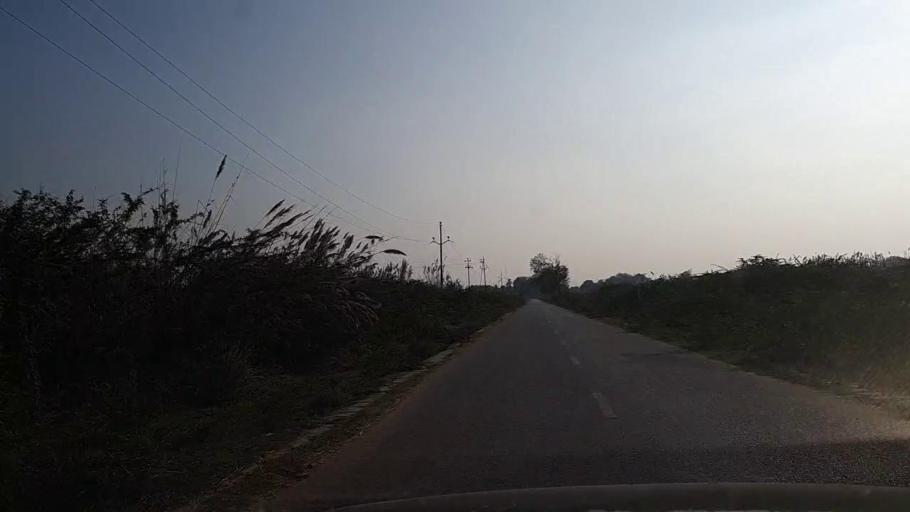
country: PK
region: Sindh
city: Gharo
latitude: 24.7819
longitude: 67.5118
